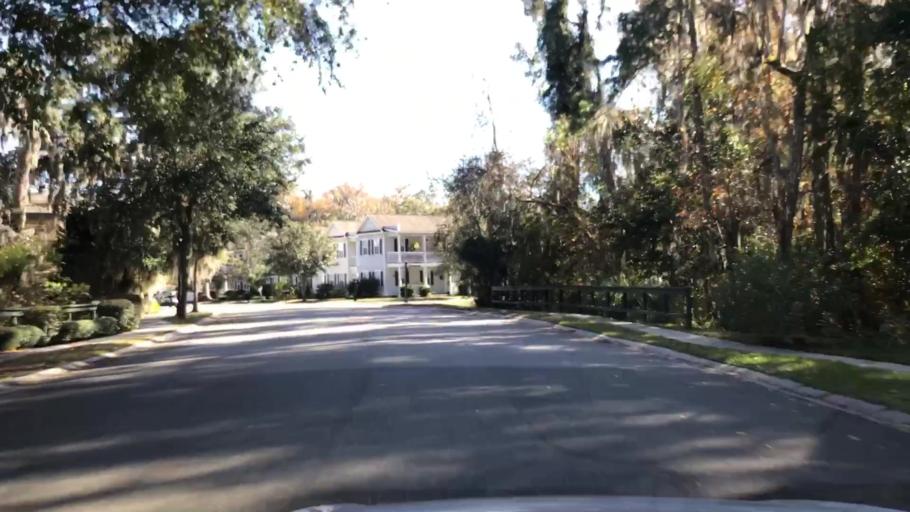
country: US
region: South Carolina
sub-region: Beaufort County
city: Bluffton
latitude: 32.2692
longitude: -80.8750
